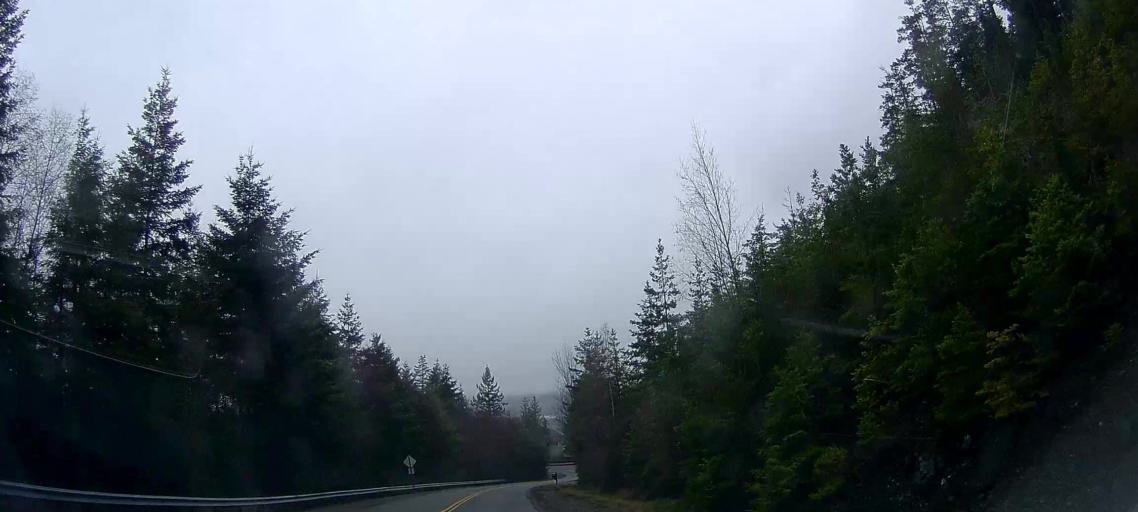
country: US
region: Washington
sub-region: Skagit County
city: Big Lake
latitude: 48.3774
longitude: -122.2895
